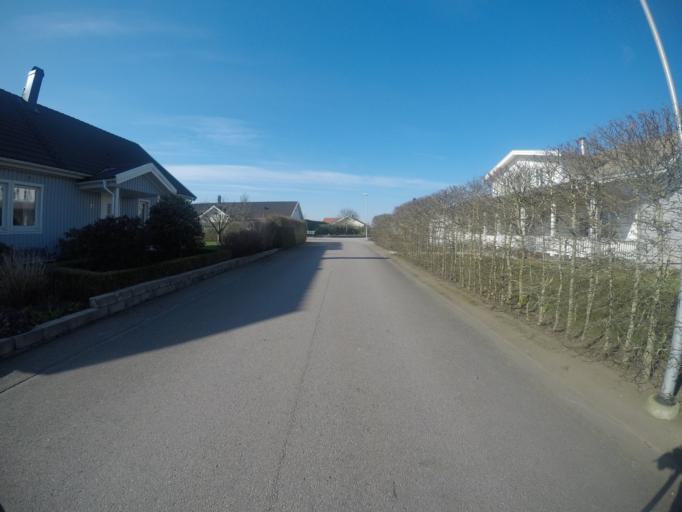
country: SE
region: Halland
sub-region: Laholms Kommun
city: Laholm
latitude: 56.5057
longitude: 13.0630
